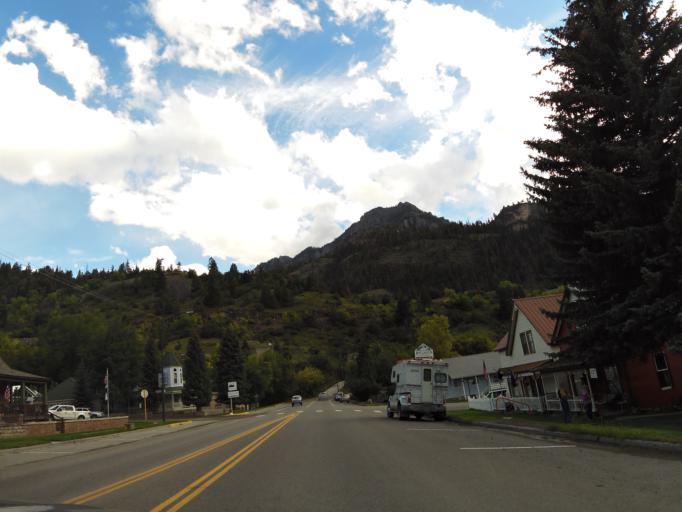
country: US
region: Colorado
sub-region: Ouray County
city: Ouray
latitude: 38.0200
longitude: -107.6715
